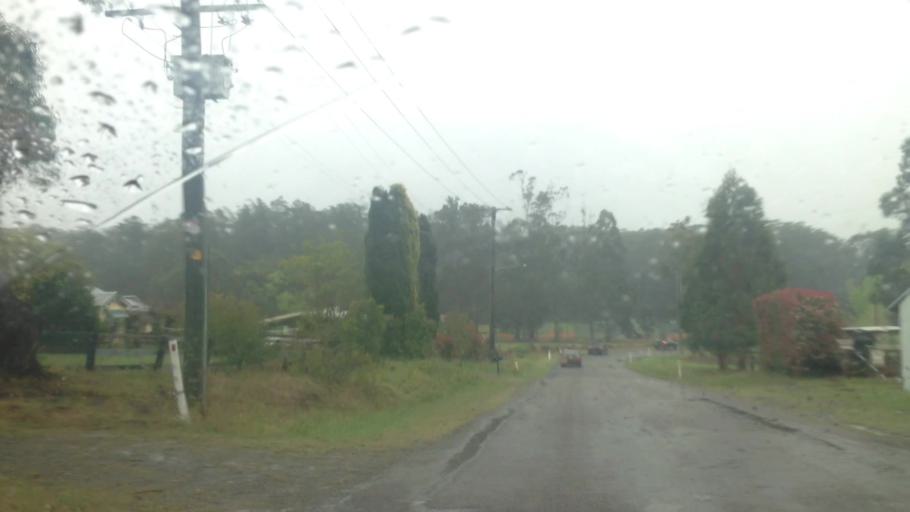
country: AU
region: New South Wales
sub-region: Wyong Shire
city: Little Jilliby
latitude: -33.1912
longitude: 151.3556
